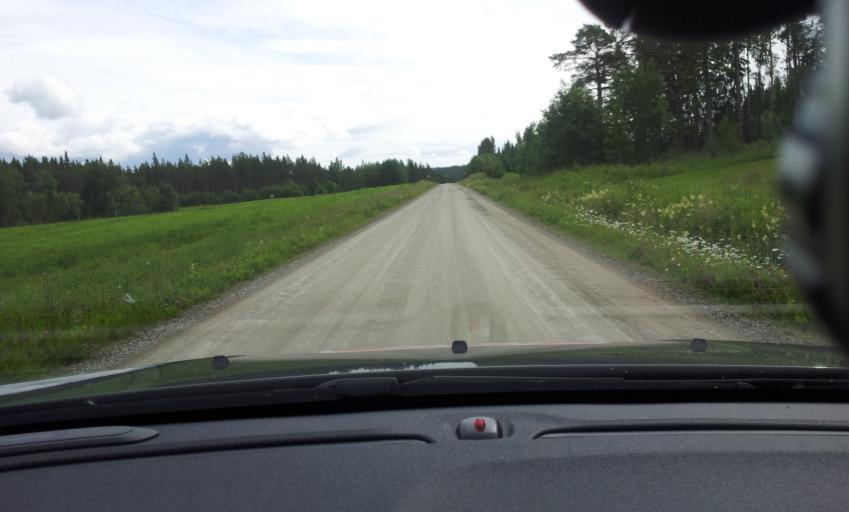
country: SE
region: Jaemtland
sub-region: OEstersunds Kommun
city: Brunflo
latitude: 62.9535
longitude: 14.9270
